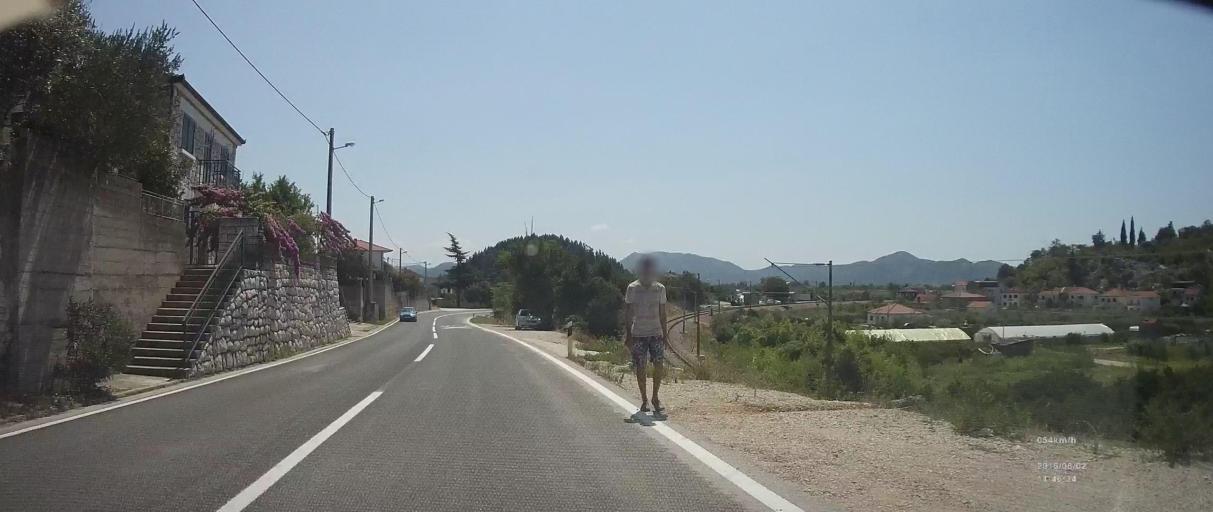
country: HR
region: Dubrovacko-Neretvanska
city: Komin
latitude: 43.0513
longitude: 17.4769
